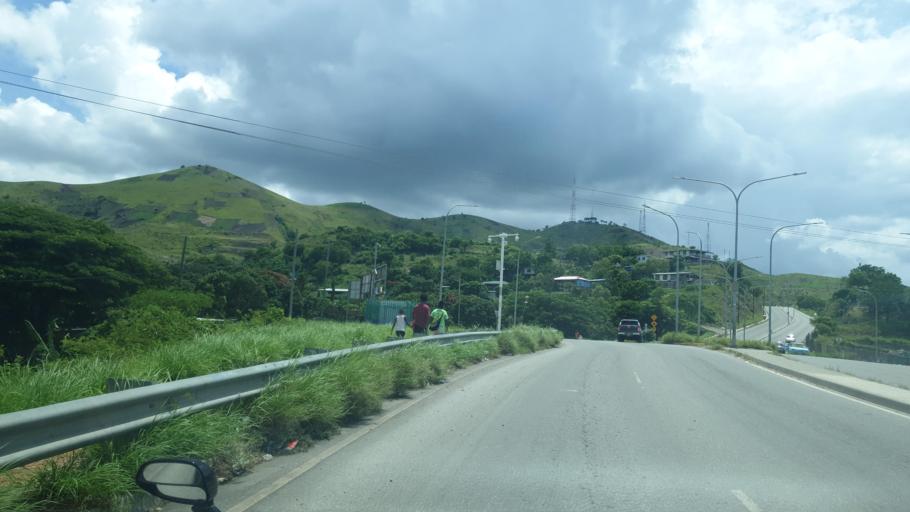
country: PG
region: National Capital
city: Port Moresby
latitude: -9.4505
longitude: 147.1526
